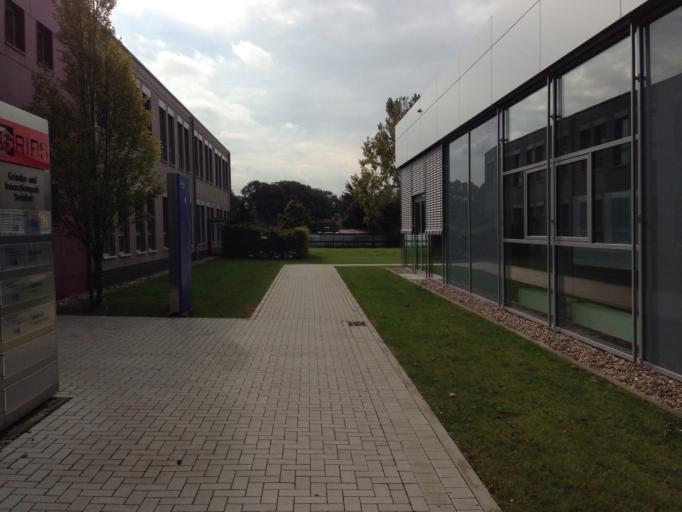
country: DE
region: North Rhine-Westphalia
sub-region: Regierungsbezirk Munster
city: Steinfurt
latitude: 52.1423
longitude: 7.3211
